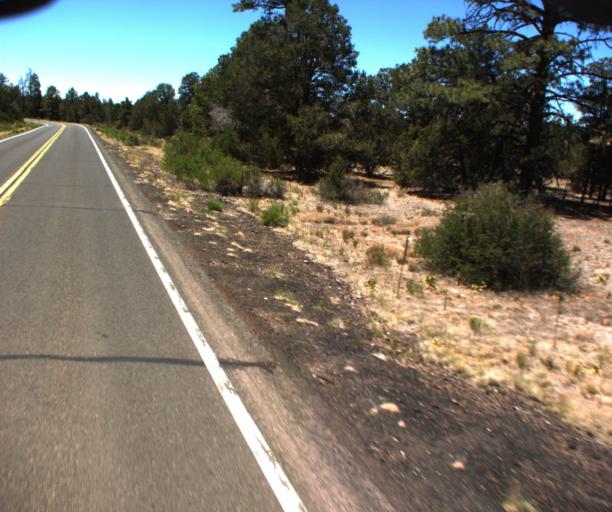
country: US
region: Arizona
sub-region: Gila County
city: Star Valley
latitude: 34.7021
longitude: -111.1037
